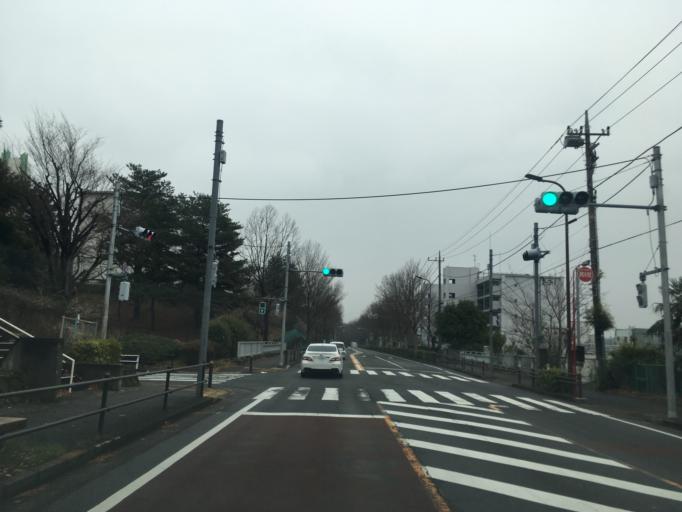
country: JP
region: Tokyo
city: Hino
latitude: 35.6330
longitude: 139.4366
